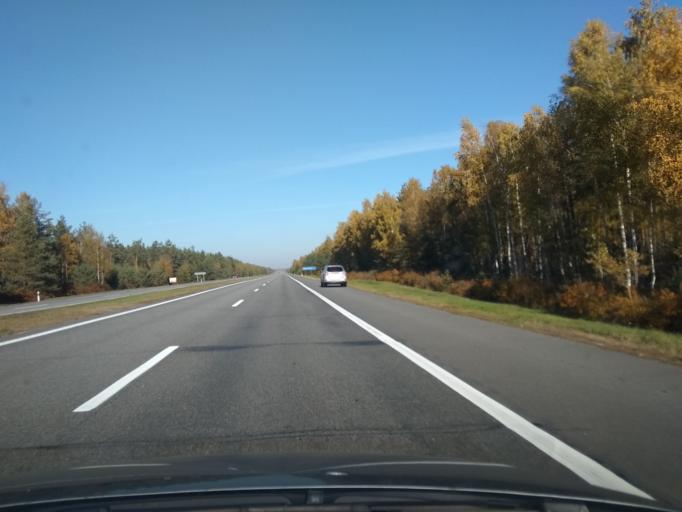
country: BY
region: Grodnenskaya
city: Zhyrovichy
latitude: 52.8944
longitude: 25.6717
